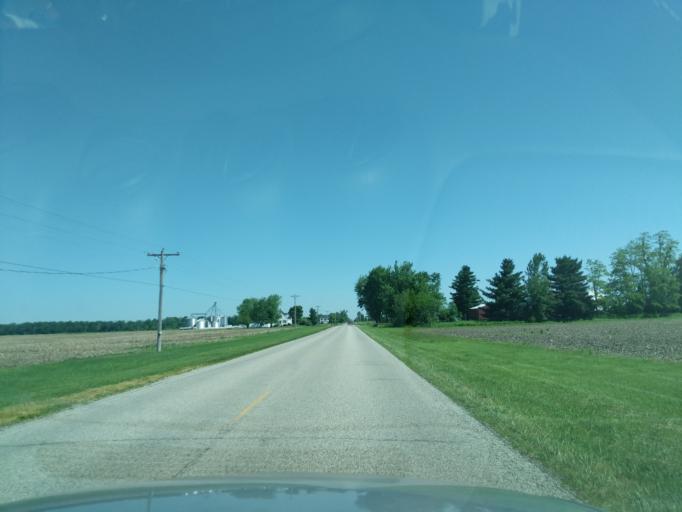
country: US
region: Indiana
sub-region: Huntington County
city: Huntington
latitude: 40.7933
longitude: -85.5078
